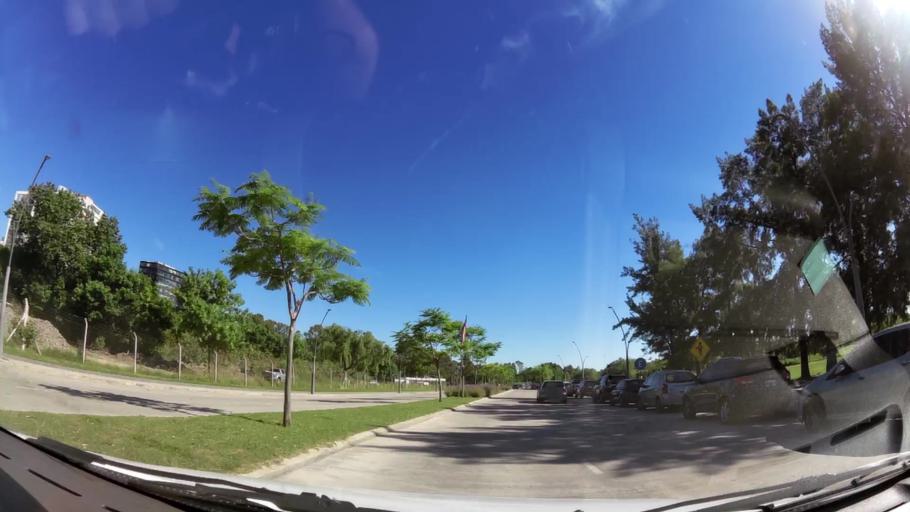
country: AR
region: Buenos Aires
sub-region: Partido de Vicente Lopez
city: Olivos
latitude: -34.5171
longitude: -58.4723
